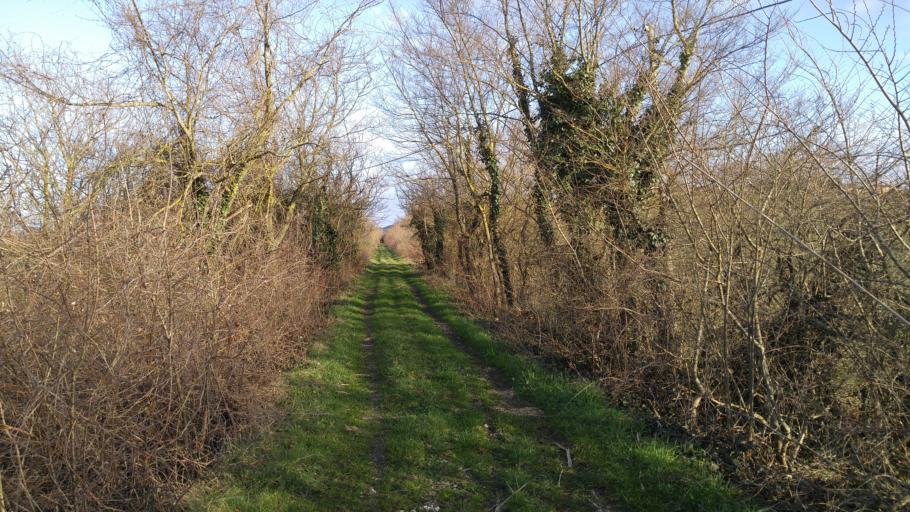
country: IT
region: The Marches
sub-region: Provincia di Pesaro e Urbino
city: Cagli
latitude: 43.5401
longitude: 12.6815
